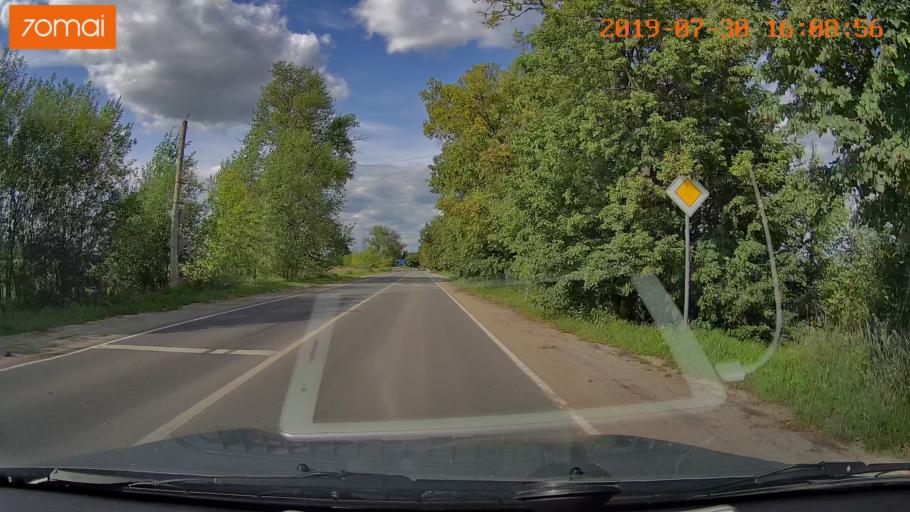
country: RU
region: Moskovskaya
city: Peski
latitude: 55.2496
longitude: 38.7193
